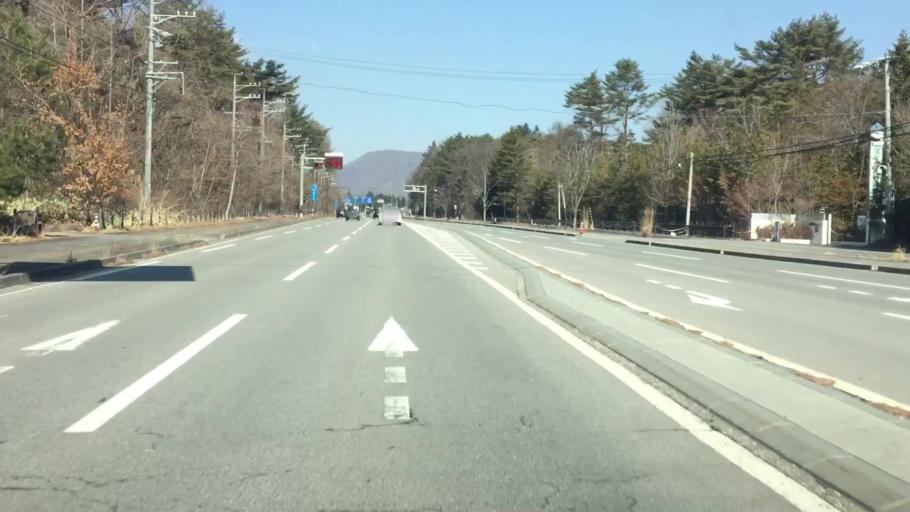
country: JP
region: Nagano
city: Saku
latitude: 36.3201
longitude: 138.6306
